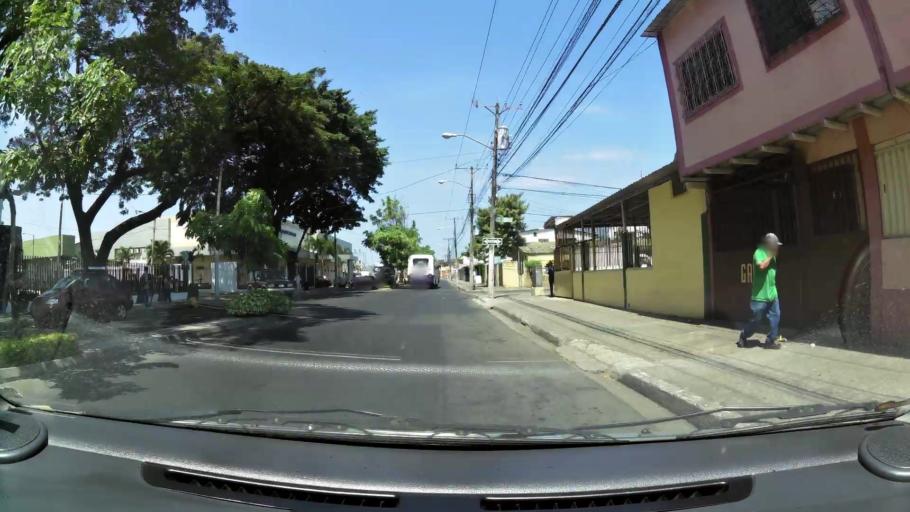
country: EC
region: Guayas
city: Guayaquil
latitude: -2.2343
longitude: -79.8992
